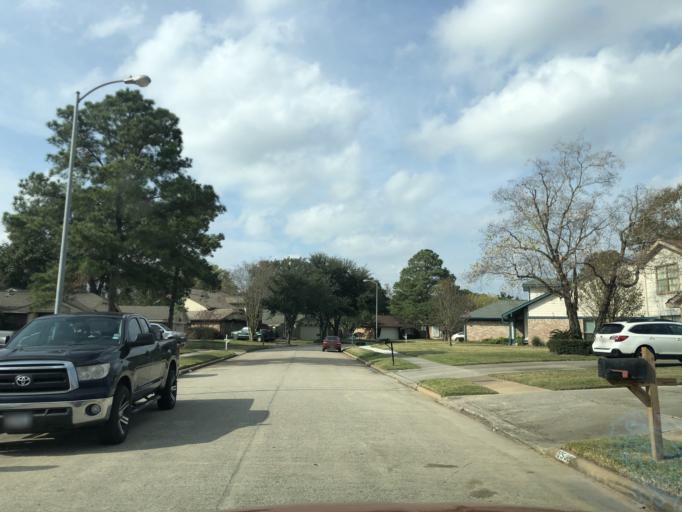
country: US
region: Texas
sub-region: Harris County
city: Tomball
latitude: 30.0371
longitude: -95.5426
